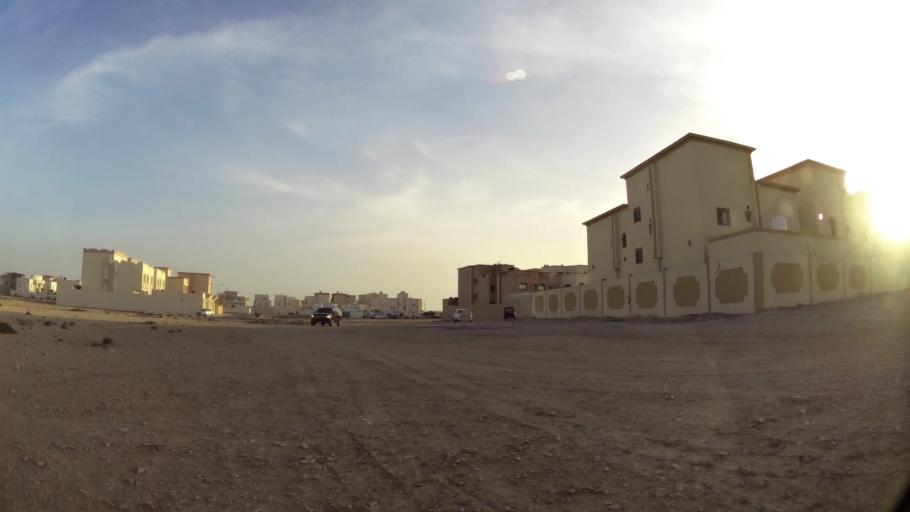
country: QA
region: Al Wakrah
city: Al Wakrah
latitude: 25.1466
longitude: 51.6130
